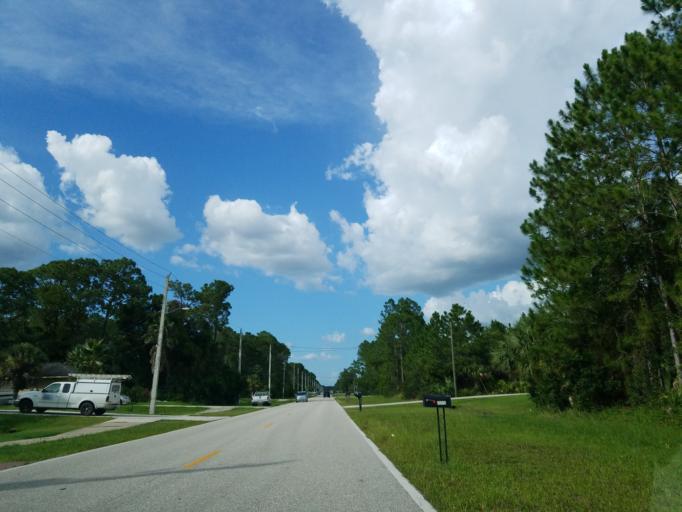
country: US
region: Florida
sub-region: Sarasota County
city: North Port
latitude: 27.0845
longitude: -82.1822
